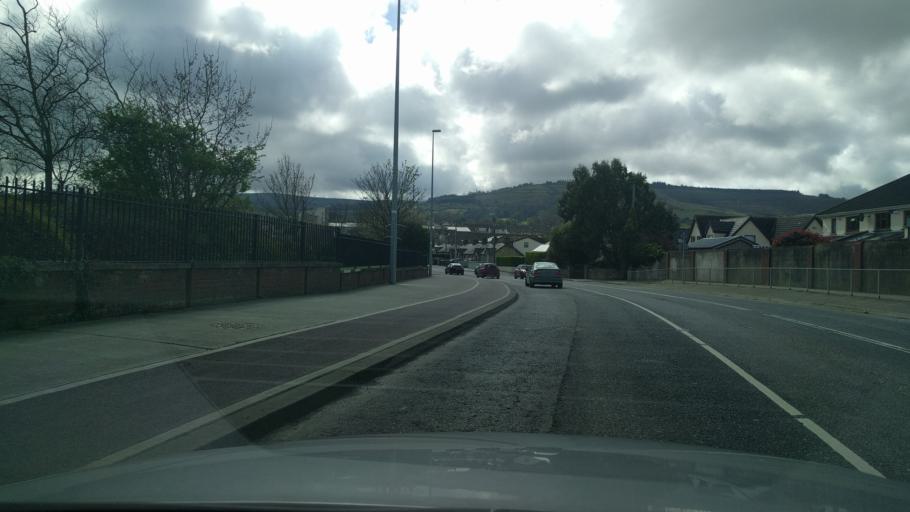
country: IE
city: Knocklyon
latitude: 53.2745
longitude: -6.3310
